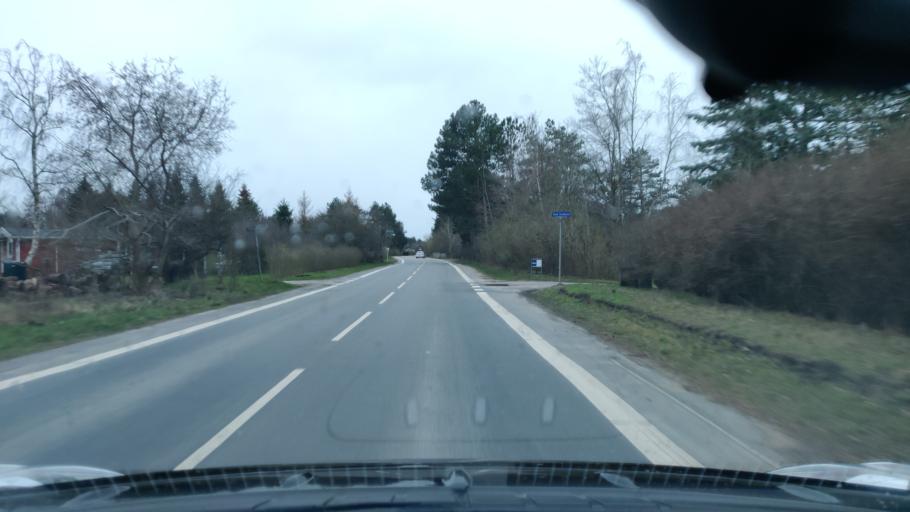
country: DK
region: Zealand
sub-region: Odsherred Kommune
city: Asnaes
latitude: 55.8688
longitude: 11.5376
